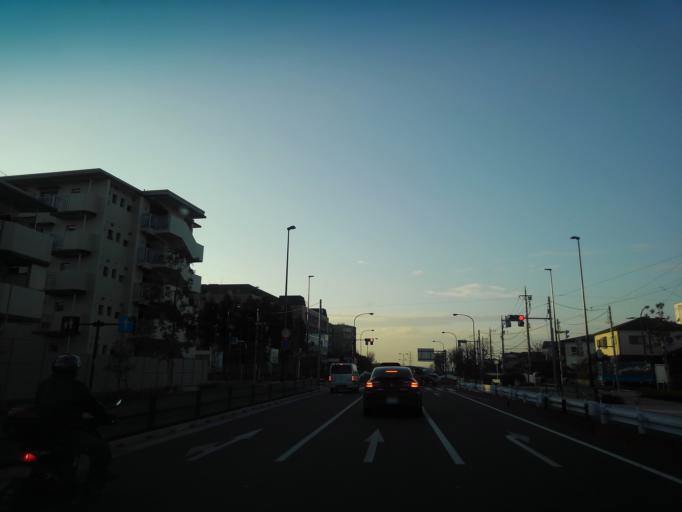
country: JP
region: Tokyo
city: Kokubunji
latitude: 35.6948
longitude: 139.4600
